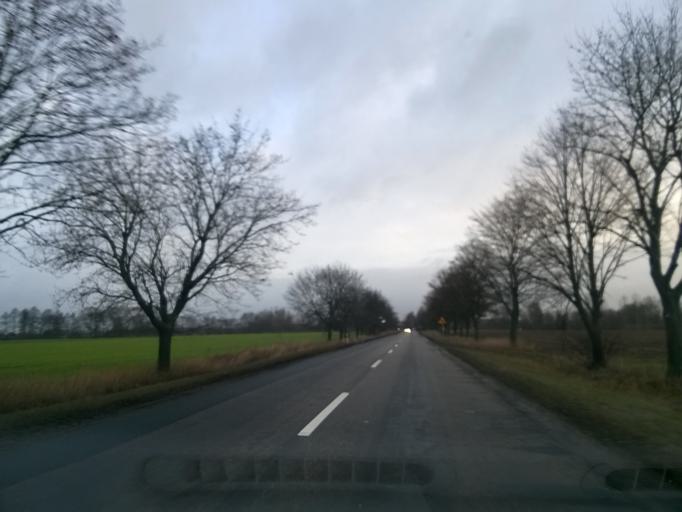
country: PL
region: Greater Poland Voivodeship
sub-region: Powiat wagrowiecki
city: Wagrowiec
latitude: 52.8486
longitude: 17.2616
